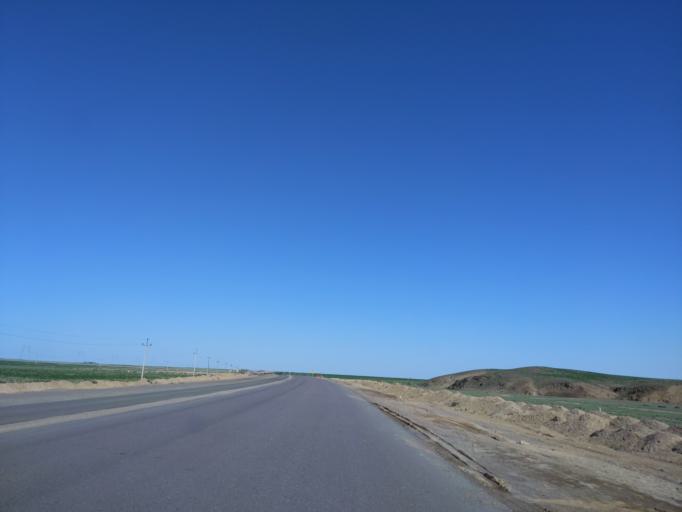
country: KZ
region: Almaty Oblysy
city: Bakanas
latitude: 44.0930
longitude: 75.9896
